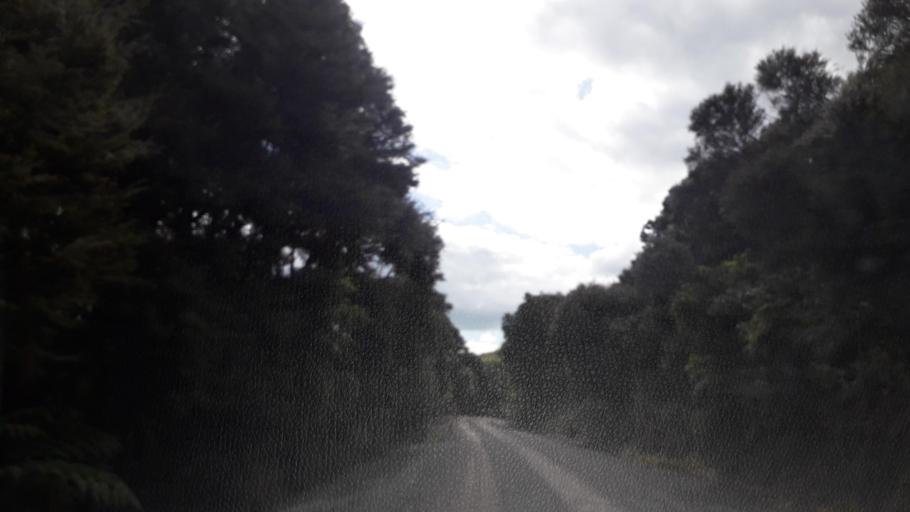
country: NZ
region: Northland
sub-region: Far North District
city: Paihia
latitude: -35.3002
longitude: 174.2198
